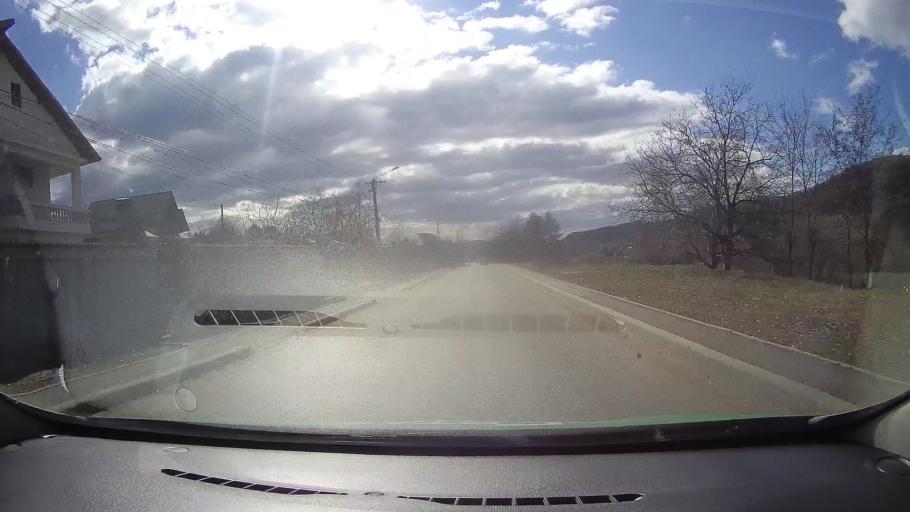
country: RO
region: Dambovita
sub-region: Oras Pucioasa
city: Pucioasa
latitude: 45.0697
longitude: 25.4303
